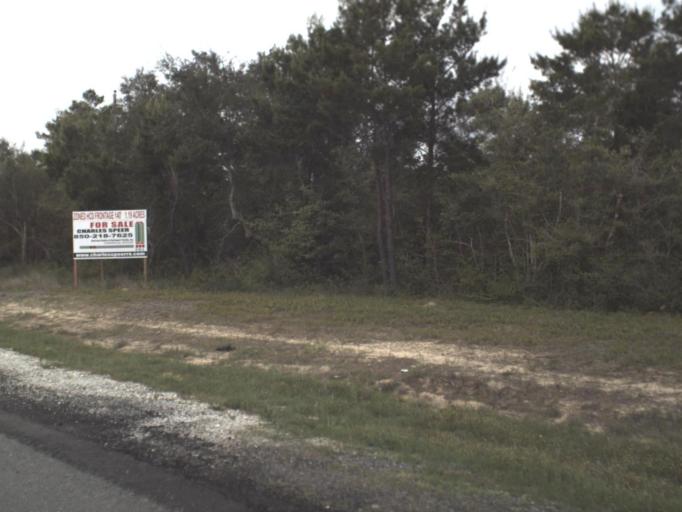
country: US
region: Florida
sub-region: Santa Rosa County
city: Woodlawn Beach
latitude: 30.3982
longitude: -87.0112
